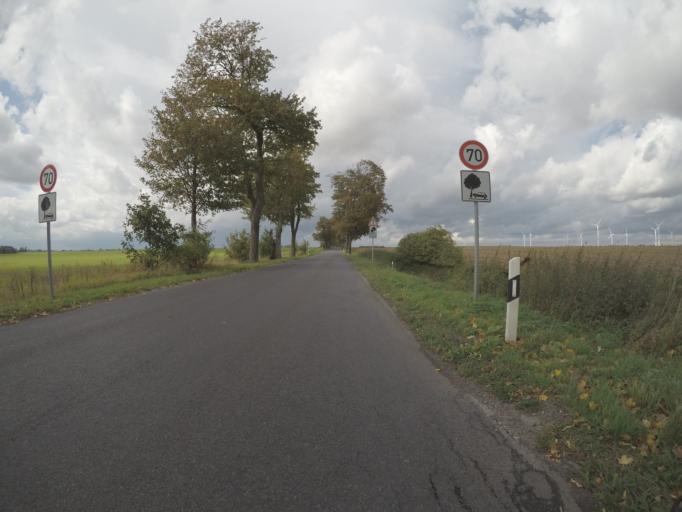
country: DE
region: Brandenburg
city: Altlandsberg
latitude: 52.5861
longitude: 13.7852
